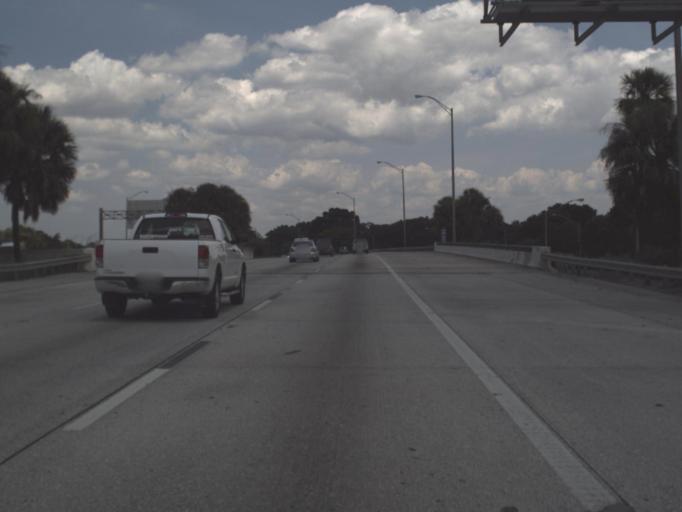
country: US
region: Florida
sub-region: Pinellas County
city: Saint Petersburg
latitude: 27.7913
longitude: -82.6603
